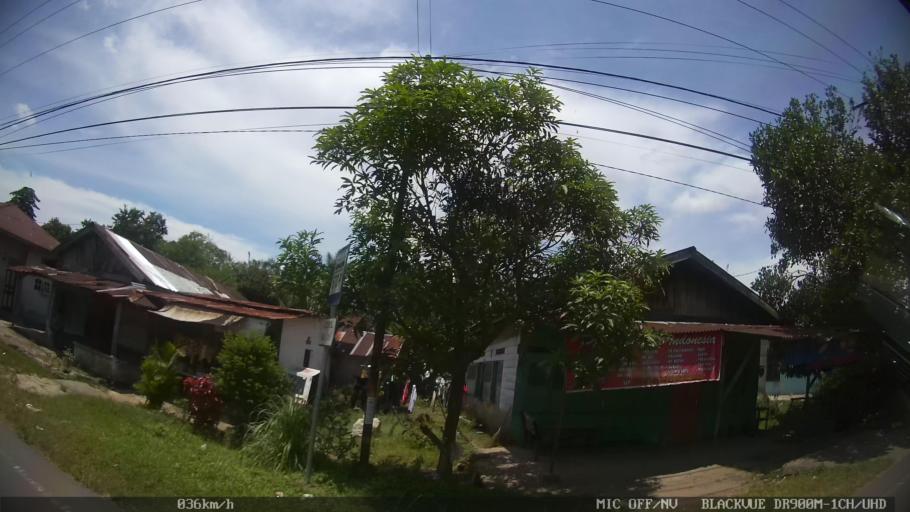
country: ID
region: North Sumatra
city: Binjai
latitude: 3.5963
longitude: 98.5005
